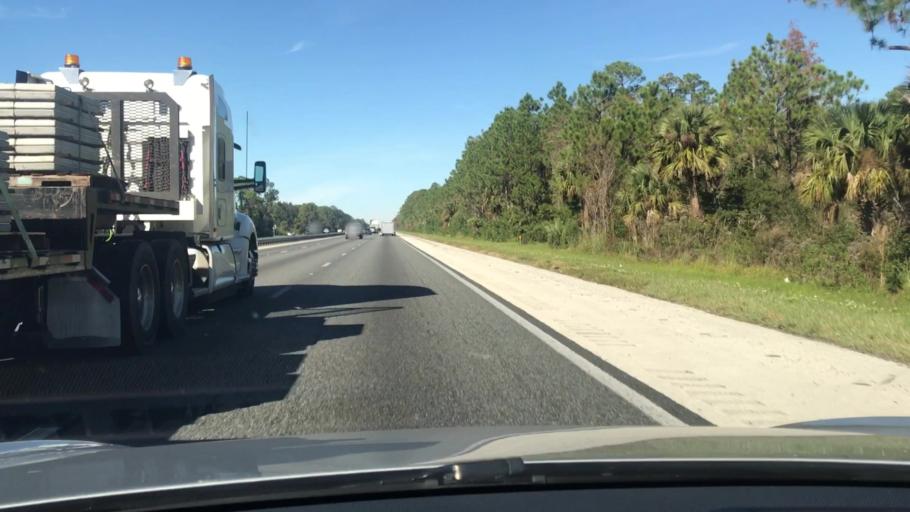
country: US
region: Florida
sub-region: Volusia County
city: Ormond-by-the-Sea
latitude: 29.3638
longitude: -81.1377
